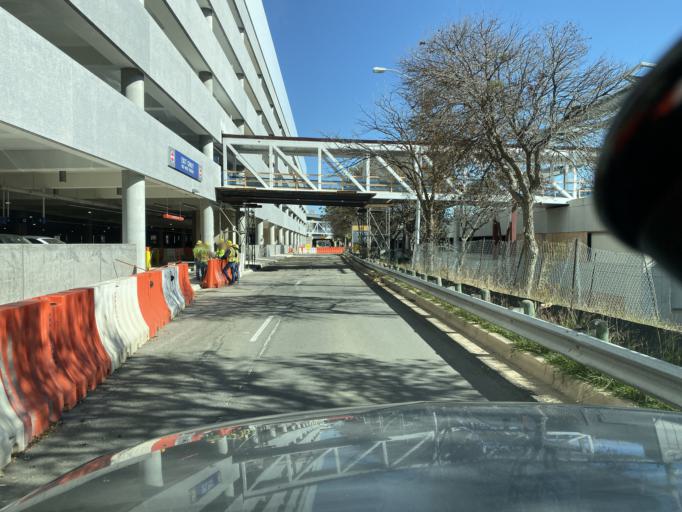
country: US
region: Texas
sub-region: Travis County
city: Hornsby Bend
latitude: 30.2042
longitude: -97.6689
